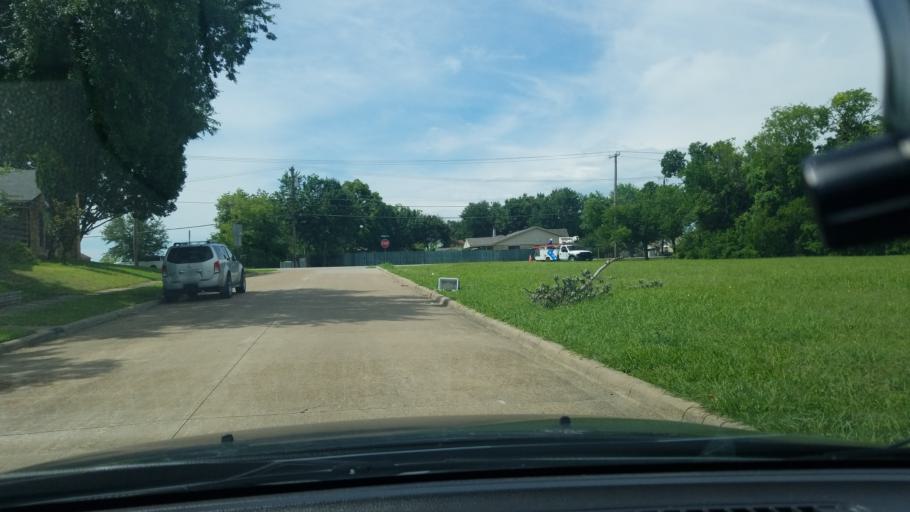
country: US
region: Texas
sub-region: Dallas County
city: Mesquite
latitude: 32.7611
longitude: -96.5785
